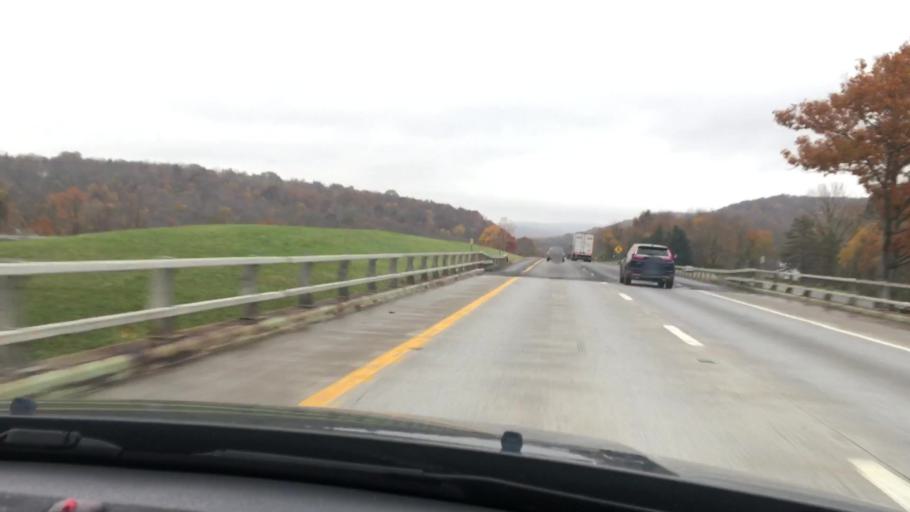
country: US
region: New York
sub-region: Putnam County
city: Lake Carmel
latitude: 41.4741
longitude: -73.6487
